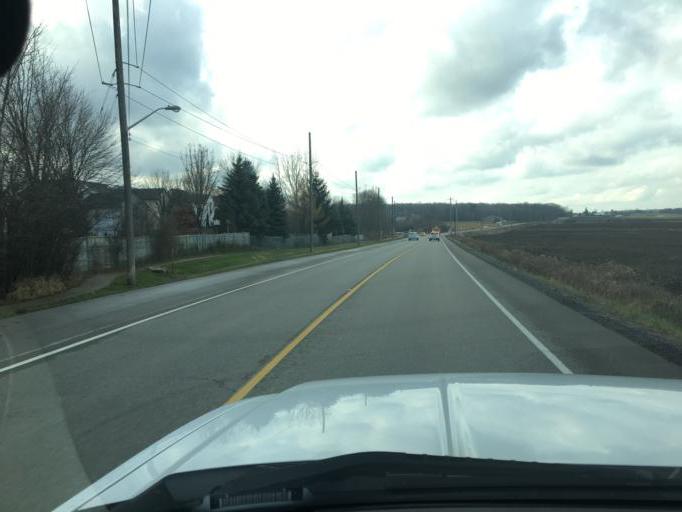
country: CA
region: Ontario
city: Waterloo
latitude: 43.4995
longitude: -80.5704
